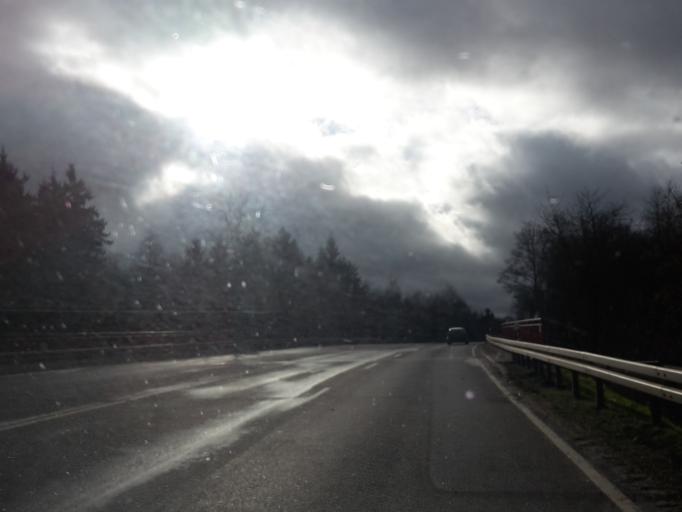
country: DE
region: Hesse
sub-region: Regierungsbezirk Darmstadt
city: Wiesbaden
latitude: 50.1360
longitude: 8.2184
